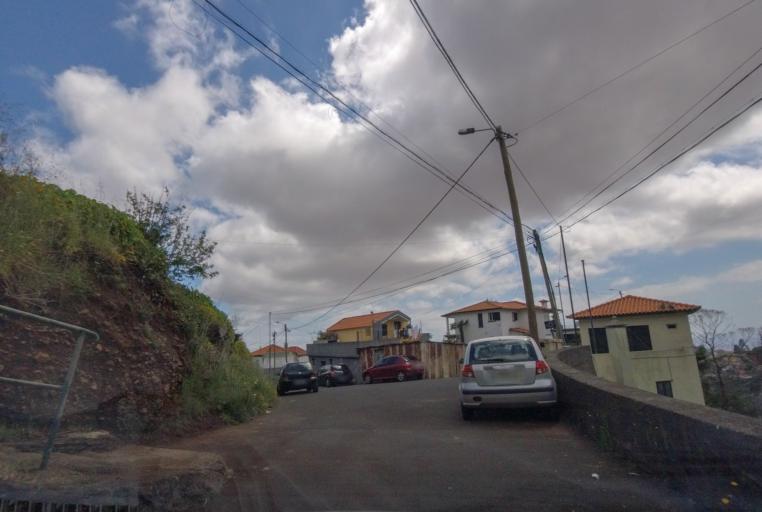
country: PT
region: Madeira
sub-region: Funchal
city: Nossa Senhora do Monte
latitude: 32.6825
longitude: -16.9128
